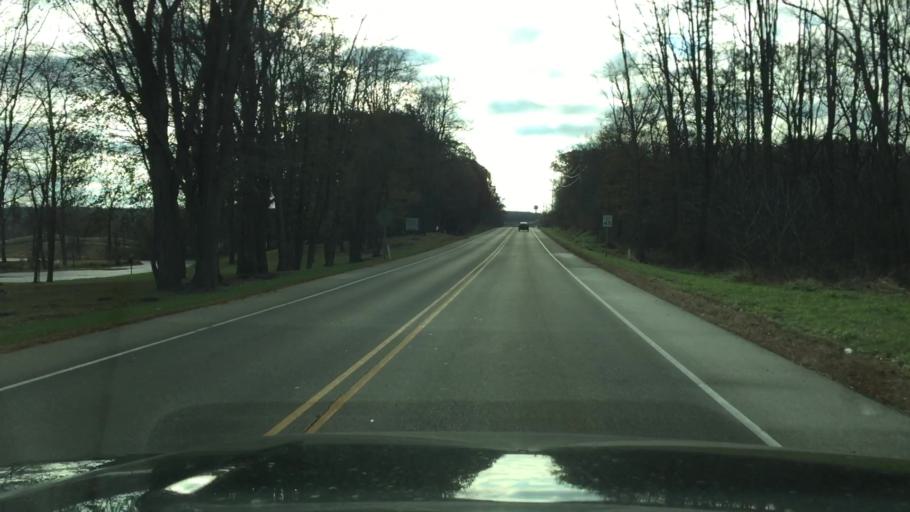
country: US
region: Wisconsin
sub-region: Walworth County
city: Williams Bay
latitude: 42.5912
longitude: -88.5332
